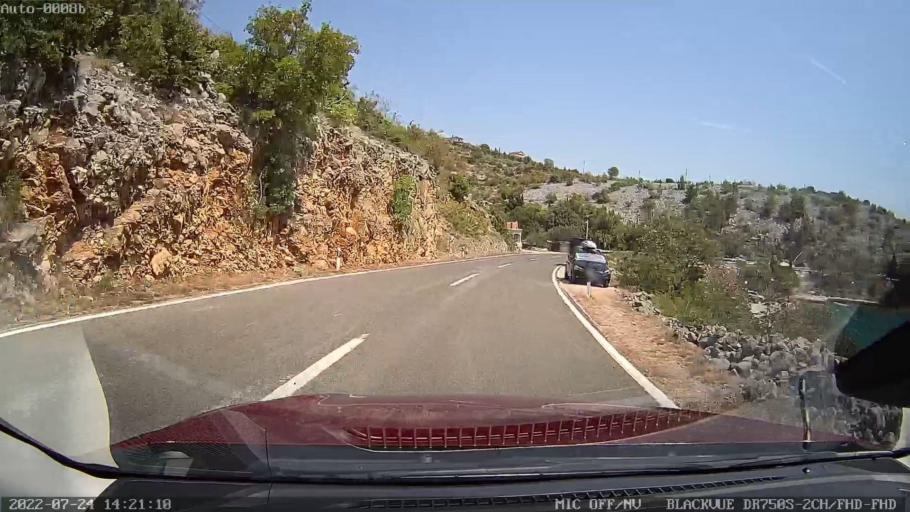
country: HR
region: Zadarska
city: Razanac
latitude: 44.3510
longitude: 15.3113
